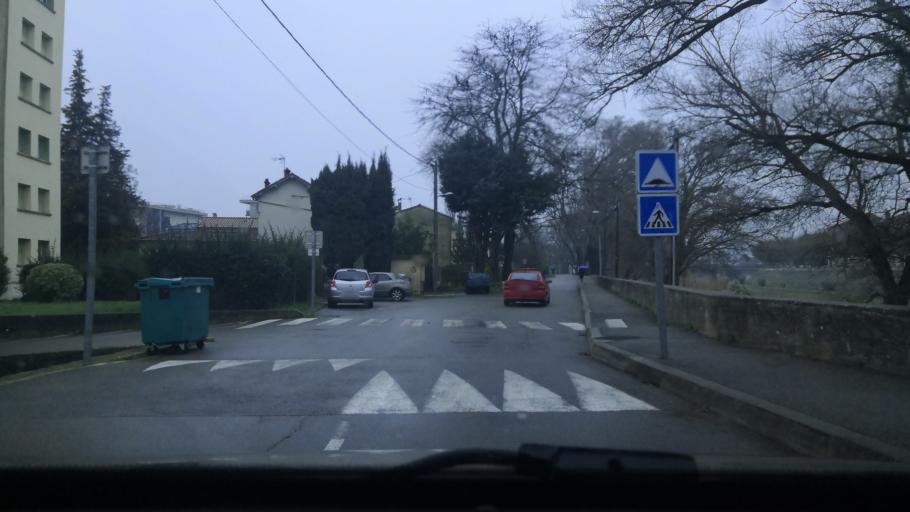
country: FR
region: Rhone-Alpes
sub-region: Departement de la Drome
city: Montelimar
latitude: 44.5541
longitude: 4.7521
